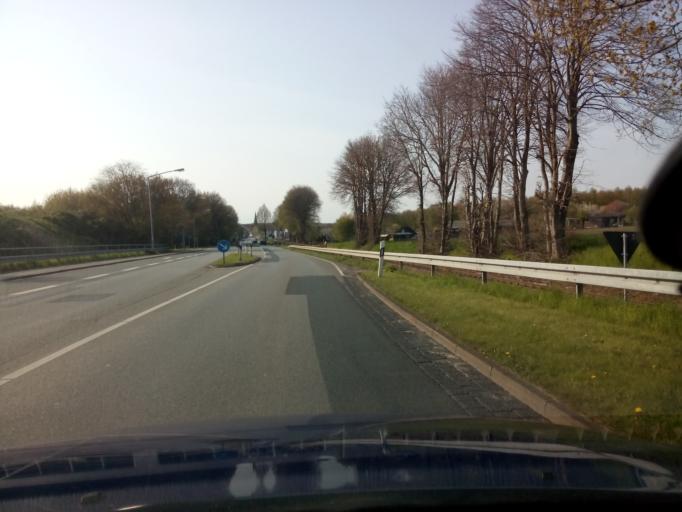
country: DE
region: Lower Saxony
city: Syke
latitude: 52.9054
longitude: 8.8383
